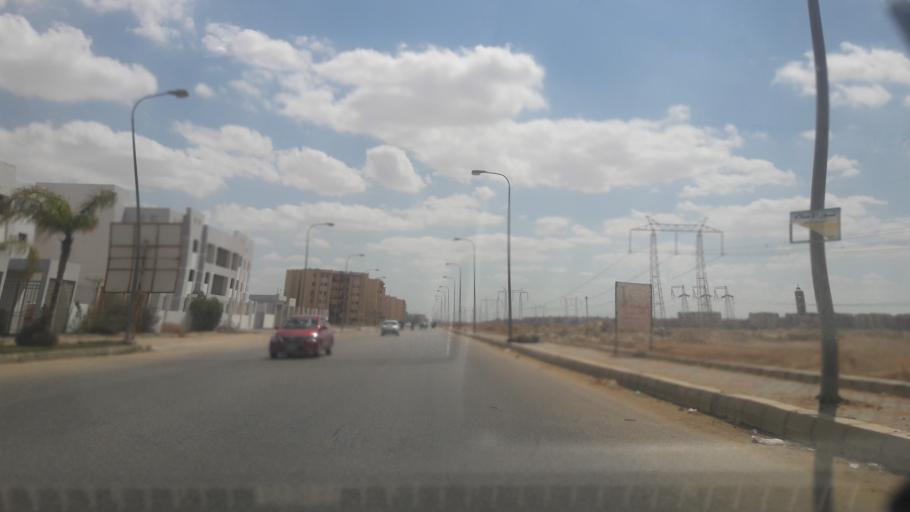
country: EG
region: Al Jizah
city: Madinat Sittah Uktubar
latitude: 29.9363
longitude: 31.0579
